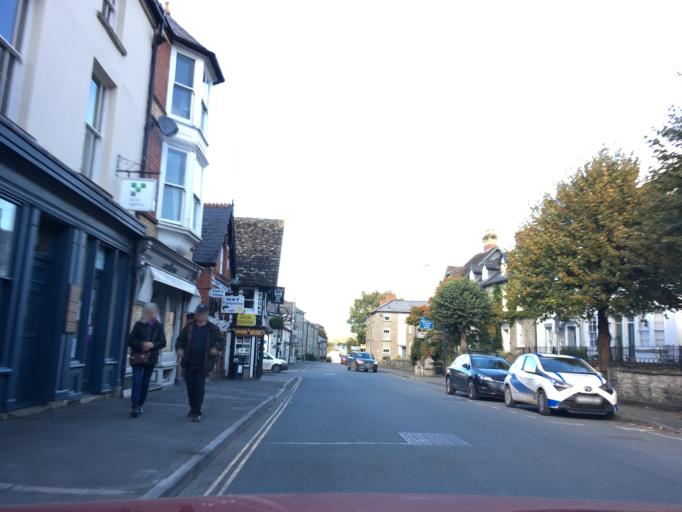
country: GB
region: Wales
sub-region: Sir Powys
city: Hay
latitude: 52.0755
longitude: -3.1260
